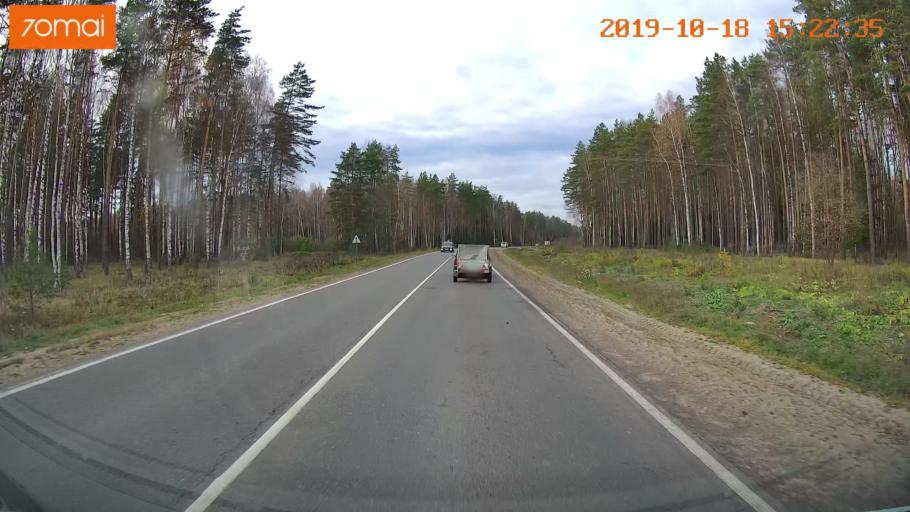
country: RU
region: Vladimir
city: Anopino
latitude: 55.7091
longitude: 40.7301
